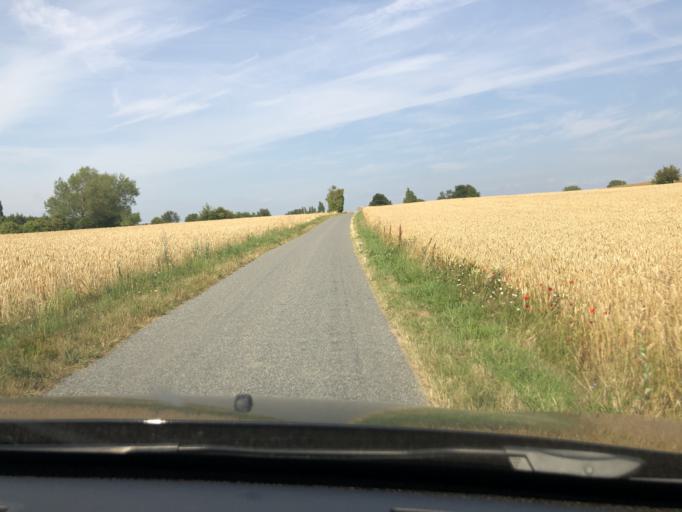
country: DK
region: South Denmark
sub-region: AEro Kommune
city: AEroskobing
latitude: 54.9268
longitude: 10.2792
